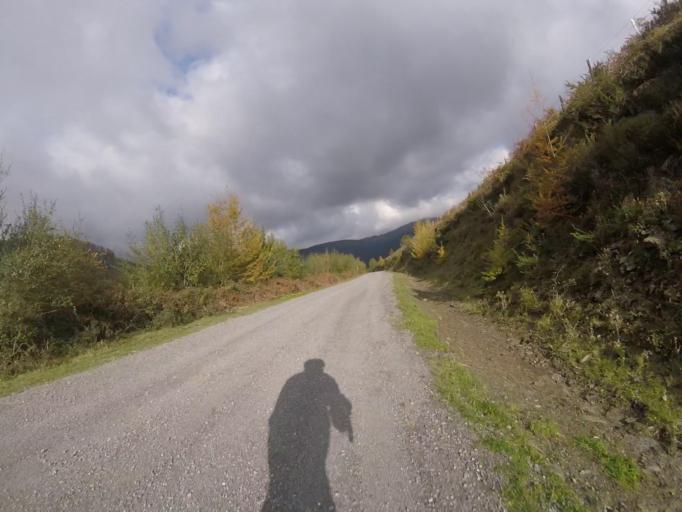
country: ES
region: Navarre
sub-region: Provincia de Navarra
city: Goizueta
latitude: 43.2119
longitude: -1.8326
